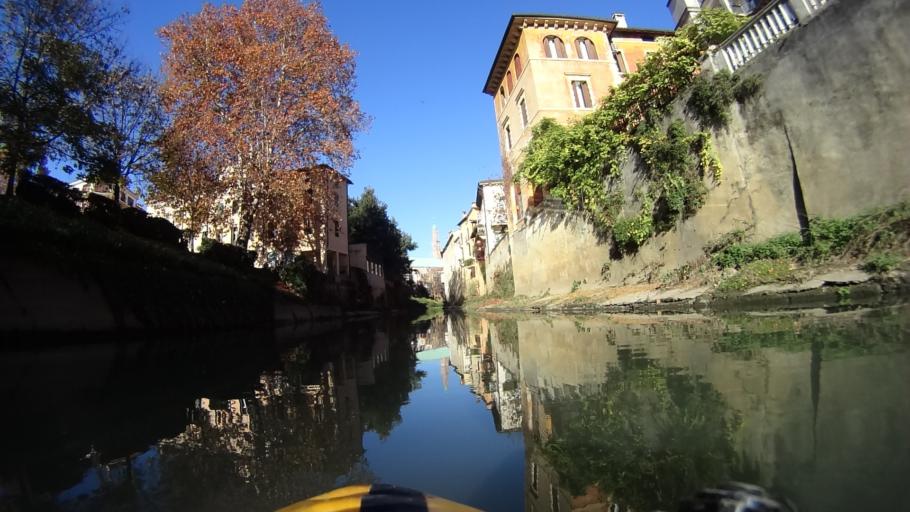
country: IT
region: Veneto
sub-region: Provincia di Vicenza
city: Vicenza
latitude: 45.5439
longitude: 11.5463
